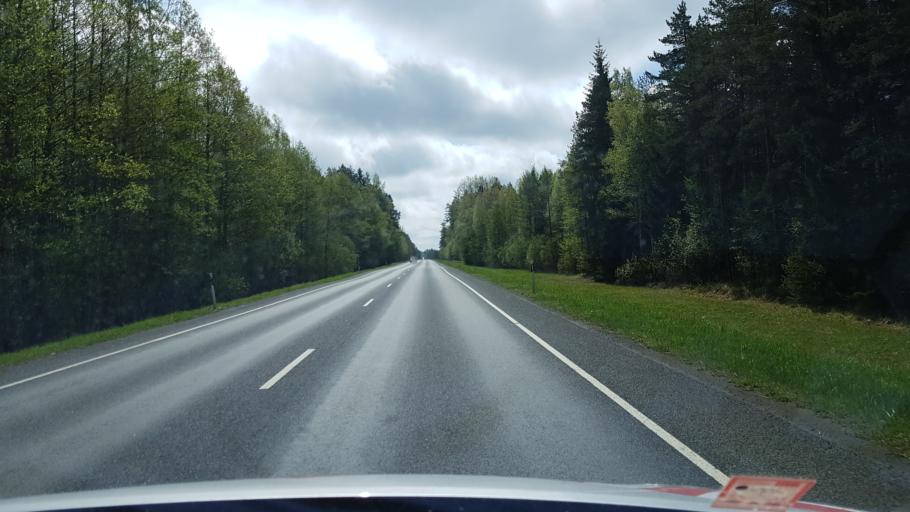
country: EE
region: Paernumaa
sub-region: Paikuse vald
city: Paikuse
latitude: 58.2479
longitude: 24.6870
